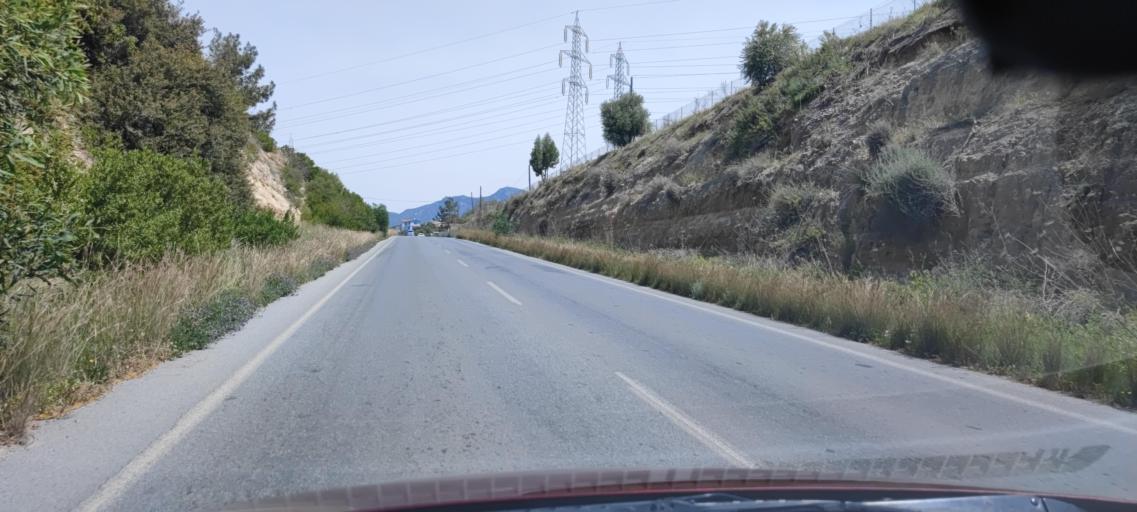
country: CY
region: Keryneia
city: Kyrenia
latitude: 35.3314
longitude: 33.4571
